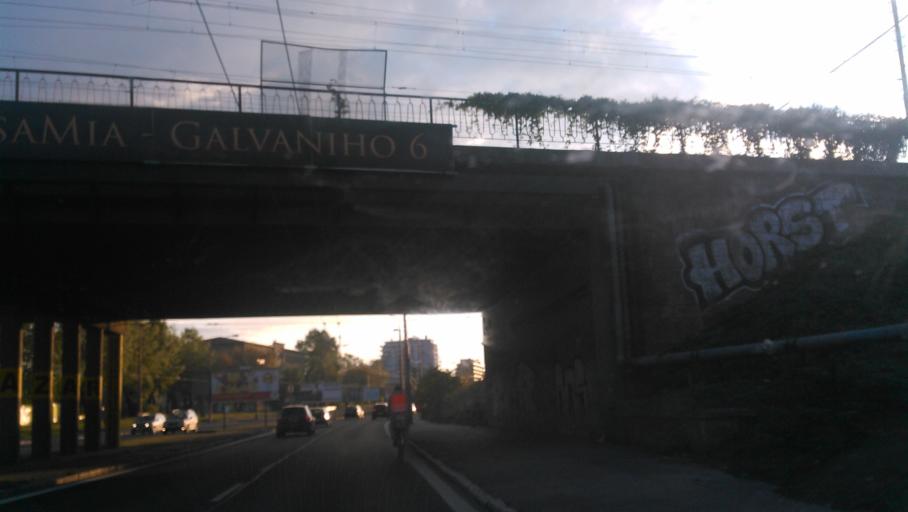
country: SK
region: Bratislavsky
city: Bratislava
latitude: 48.1680
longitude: 17.1561
